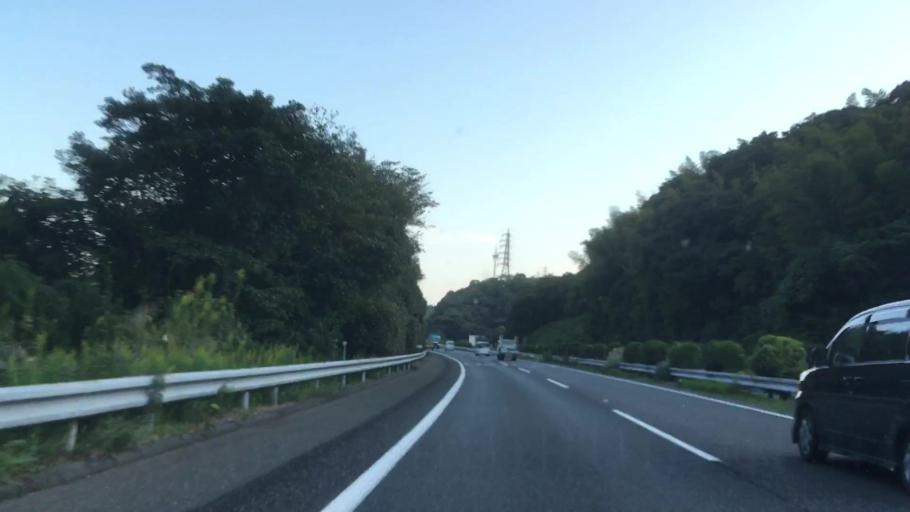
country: JP
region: Yamaguchi
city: Shimonoseki
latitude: 33.9014
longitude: 130.9714
